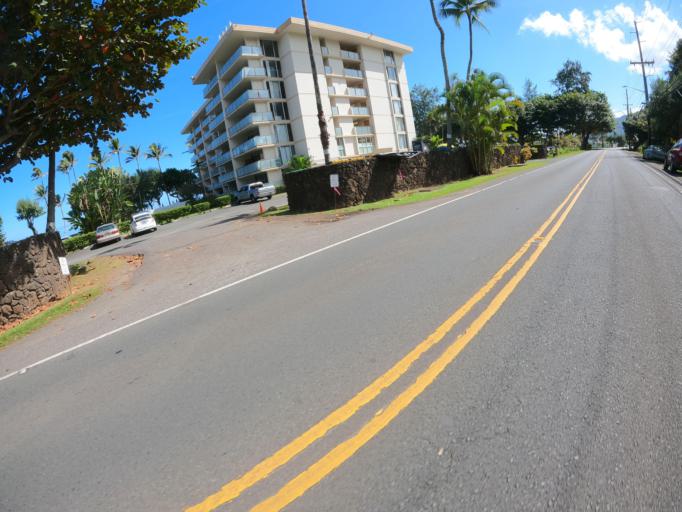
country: US
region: Hawaii
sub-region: Honolulu County
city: Punaluu
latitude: 21.5894
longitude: -157.8900
